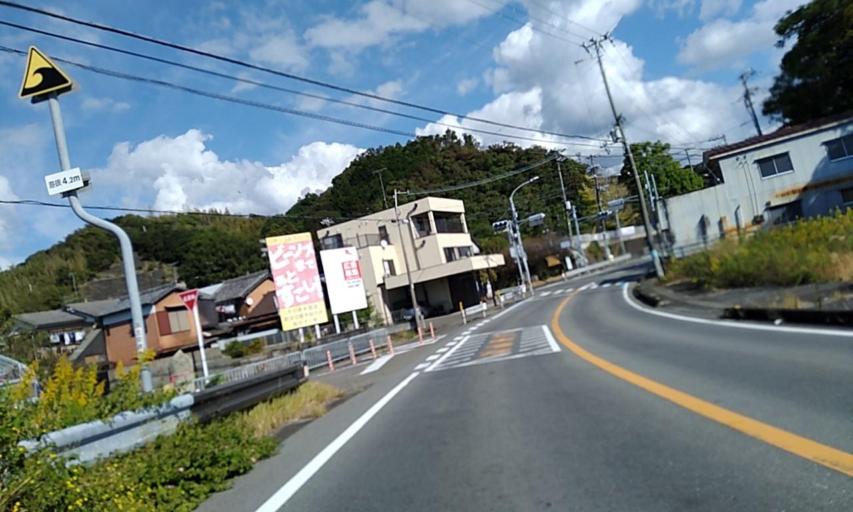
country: JP
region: Wakayama
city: Tanabe
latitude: 33.7487
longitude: 135.3517
